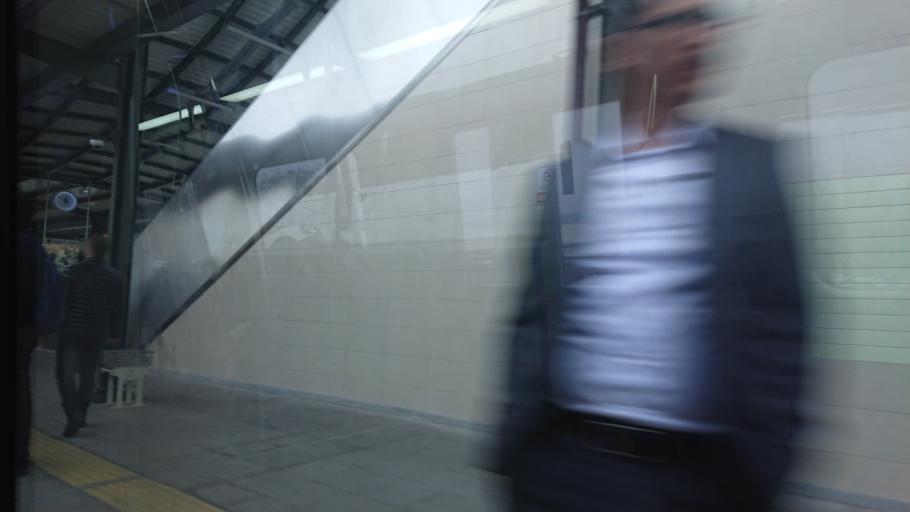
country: TR
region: Istanbul
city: Mahmutbey
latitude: 40.9888
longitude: 28.7729
